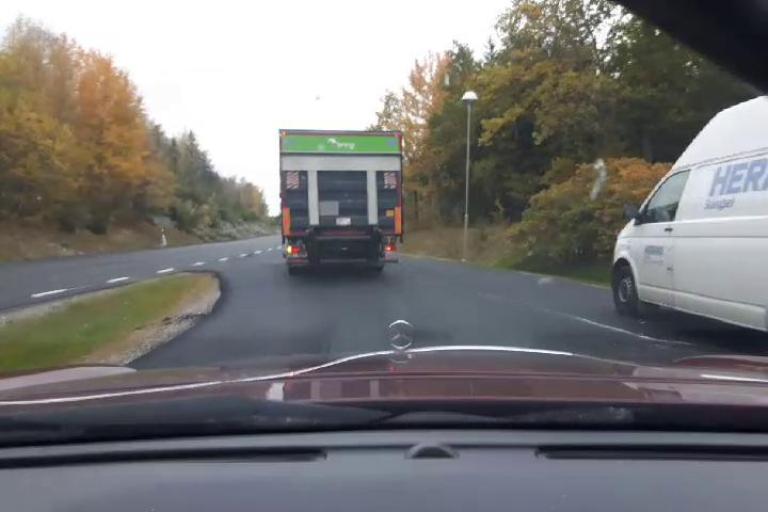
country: SE
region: Soedermanland
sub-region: Strangnas Kommun
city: Strangnas
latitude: 59.4027
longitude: 17.0192
